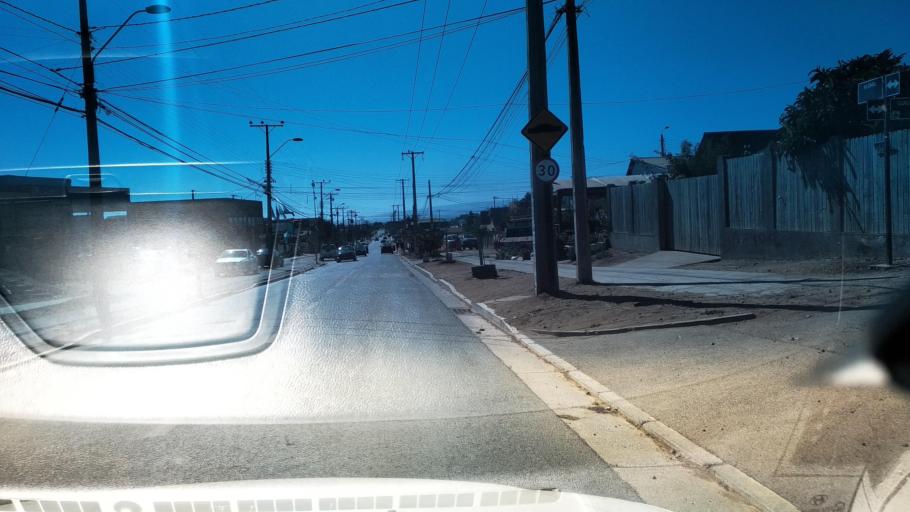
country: CL
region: O'Higgins
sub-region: Provincia de Colchagua
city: Santa Cruz
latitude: -34.3983
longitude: -71.9956
